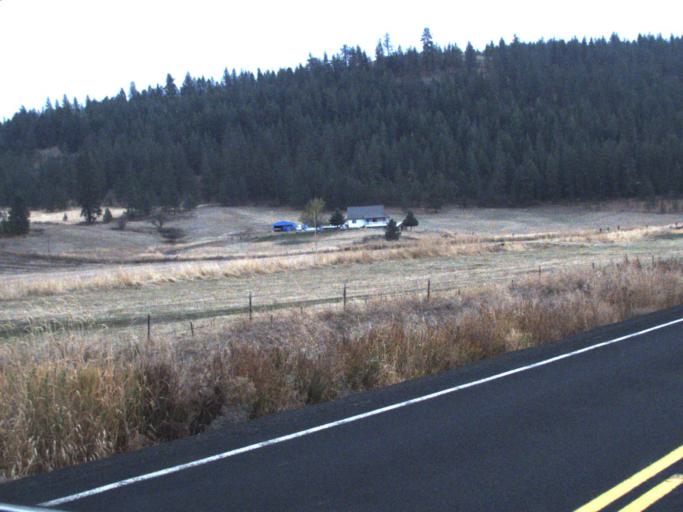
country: US
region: Washington
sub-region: Lincoln County
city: Davenport
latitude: 47.8844
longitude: -118.2643
